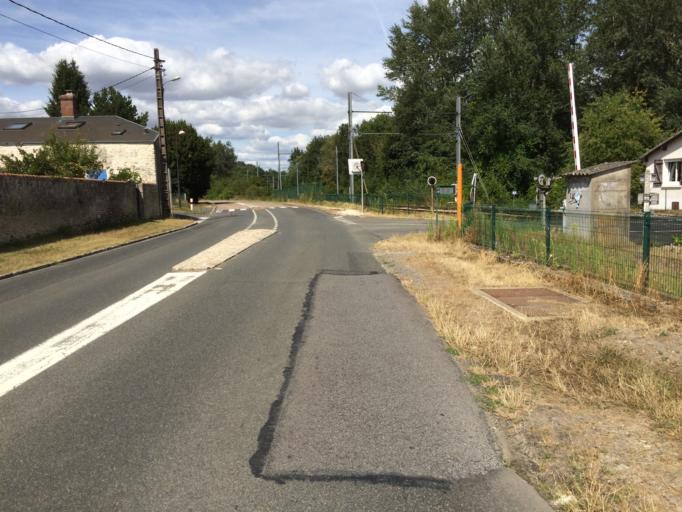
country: FR
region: Ile-de-France
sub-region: Departement de l'Essonne
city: Maisse
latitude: 48.3443
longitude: 2.3795
